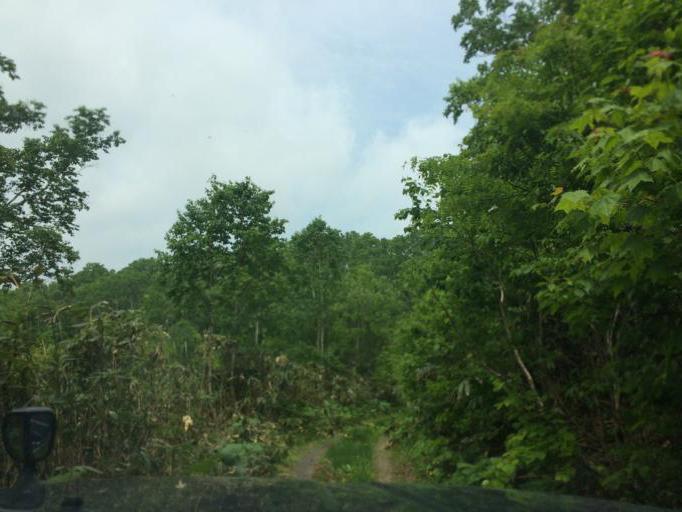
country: JP
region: Hokkaido
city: Niseko Town
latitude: 42.6841
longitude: 140.6197
